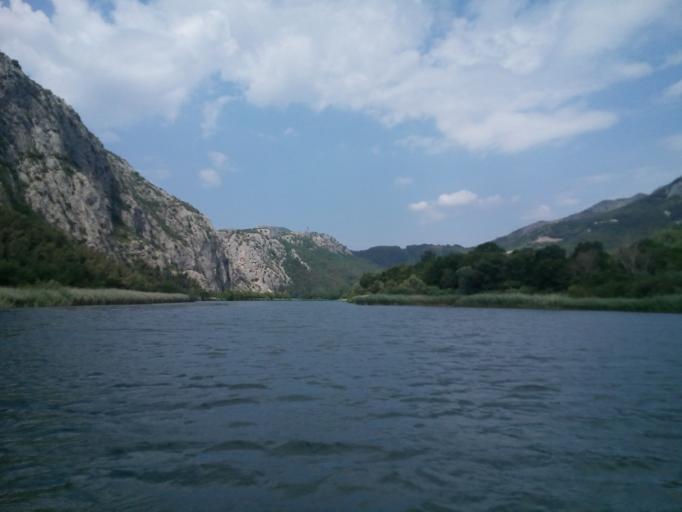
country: HR
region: Splitsko-Dalmatinska
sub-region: Grad Omis
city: Omis
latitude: 43.4500
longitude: 16.7135
